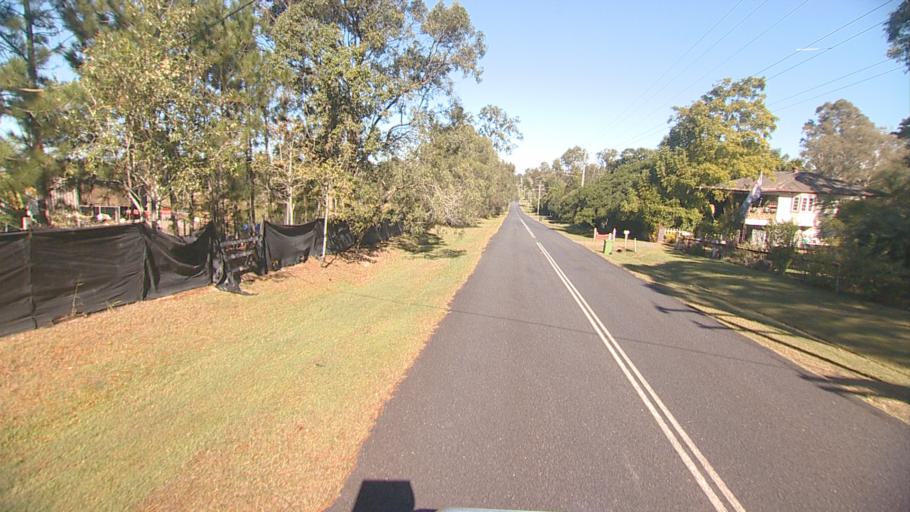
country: AU
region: Queensland
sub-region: Logan
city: Park Ridge South
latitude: -27.7143
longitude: 153.0582
